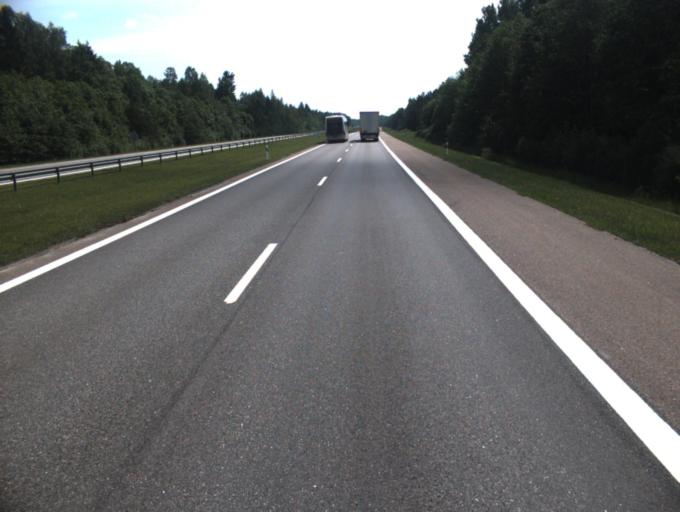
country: LT
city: Rietavas
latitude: 55.6569
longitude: 21.7768
